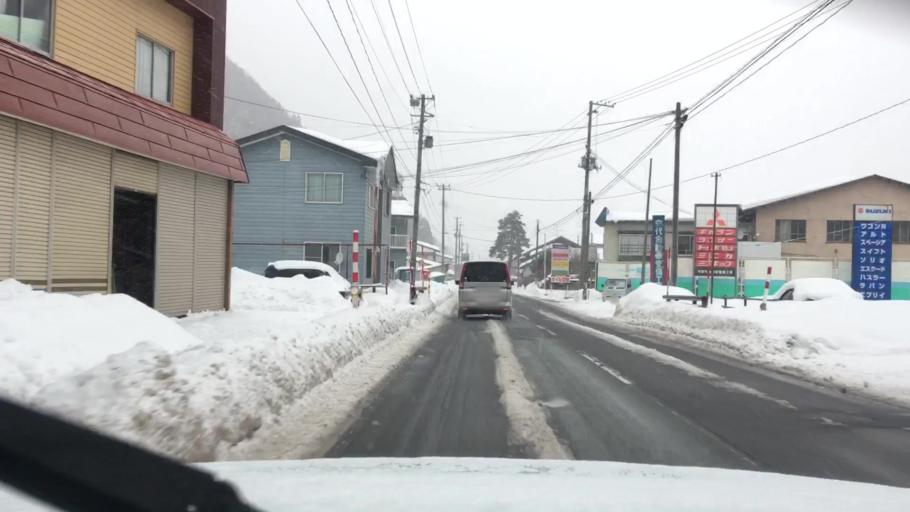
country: JP
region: Iwate
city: Ichinohe
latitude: 40.0917
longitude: 141.0469
